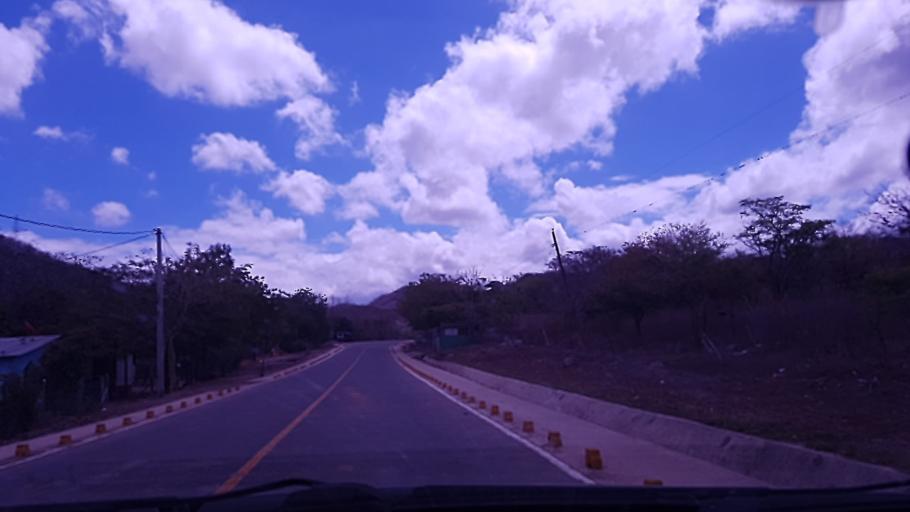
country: NI
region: Esteli
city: Condega
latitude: 13.3771
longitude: -86.3684
